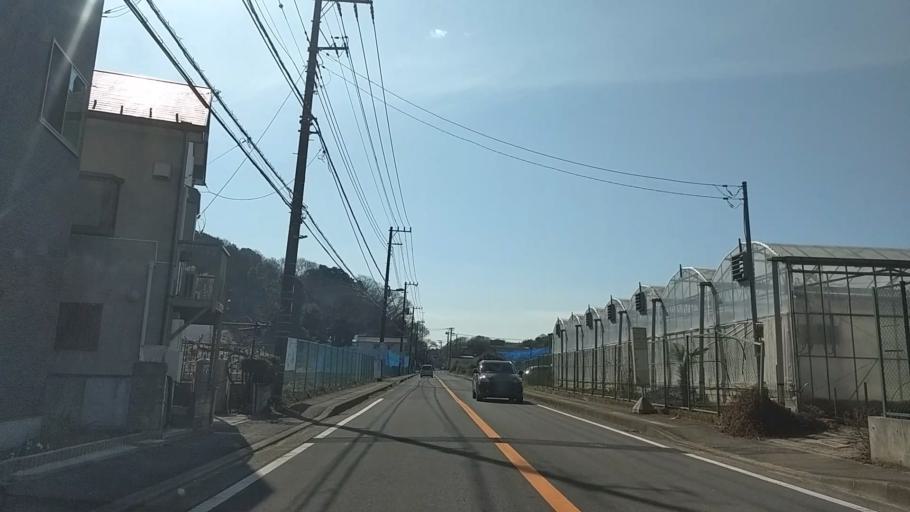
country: JP
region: Kanagawa
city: Kamakura
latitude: 35.4059
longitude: 139.5529
